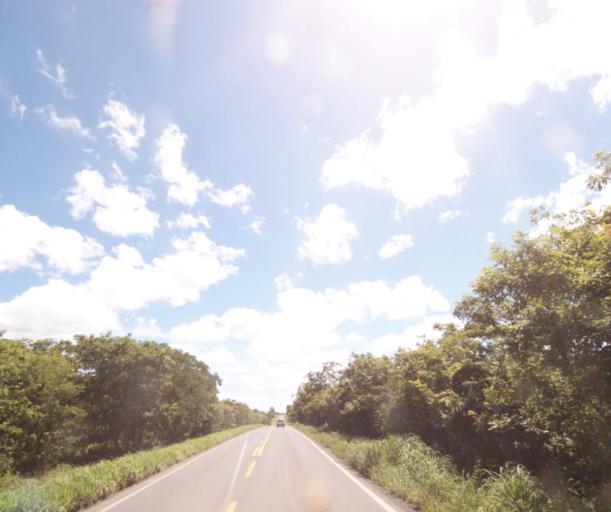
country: BR
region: Bahia
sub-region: Sao Felix Do Coribe
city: Santa Maria da Vitoria
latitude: -13.4047
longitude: -44.1536
